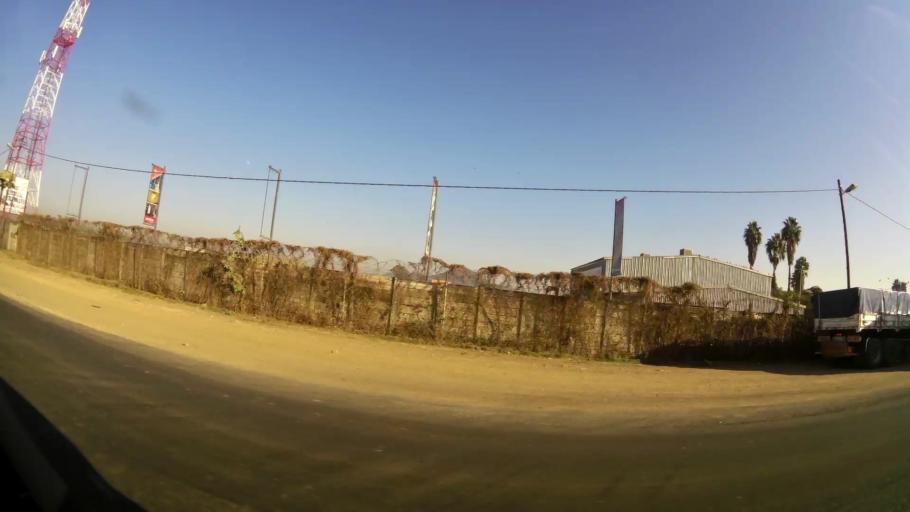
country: ZA
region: Gauteng
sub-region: City of Tshwane Metropolitan Municipality
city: Pretoria
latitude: -25.6361
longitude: 28.1996
